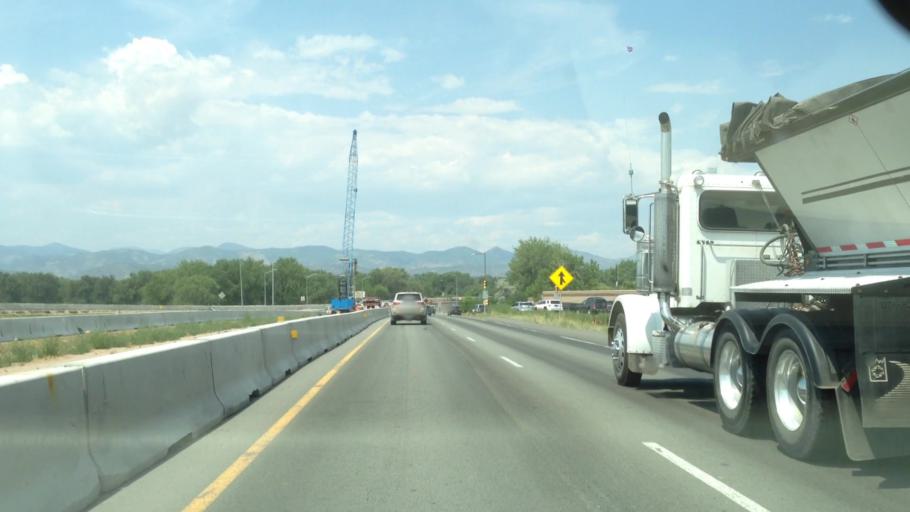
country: US
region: Colorado
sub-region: Arapahoe County
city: Columbine Valley
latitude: 39.5647
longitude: -105.0345
